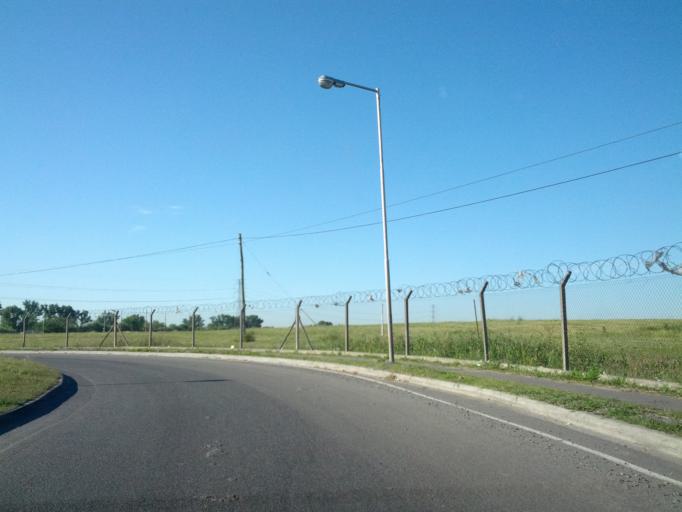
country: AR
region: Buenos Aires F.D.
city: Villa Lugano
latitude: -34.7041
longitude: -58.4638
